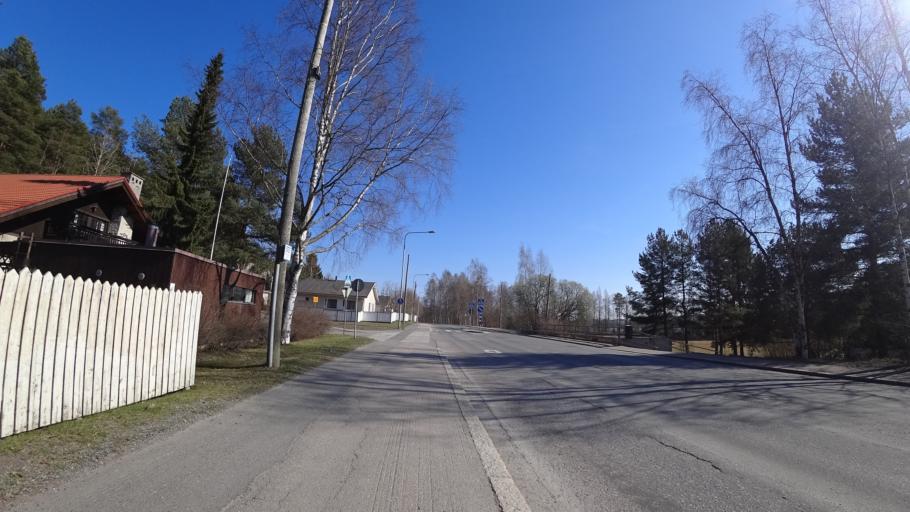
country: FI
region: Pirkanmaa
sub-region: Tampere
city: Pirkkala
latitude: 61.5145
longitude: 23.6528
